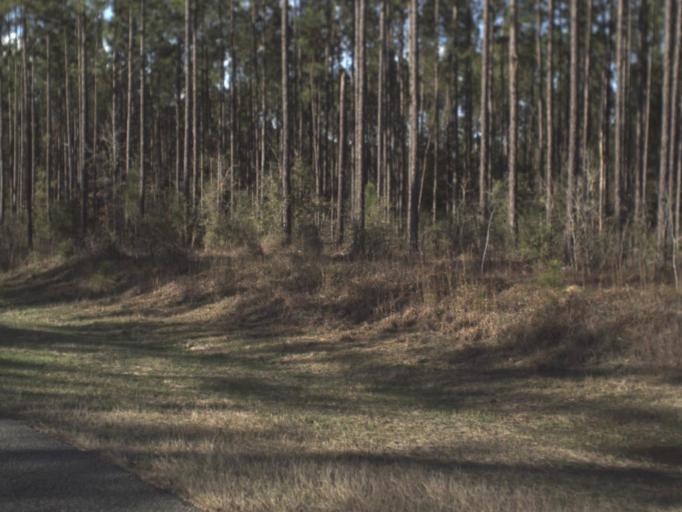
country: US
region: Florida
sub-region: Jackson County
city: Marianna
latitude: 30.6373
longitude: -85.1928
